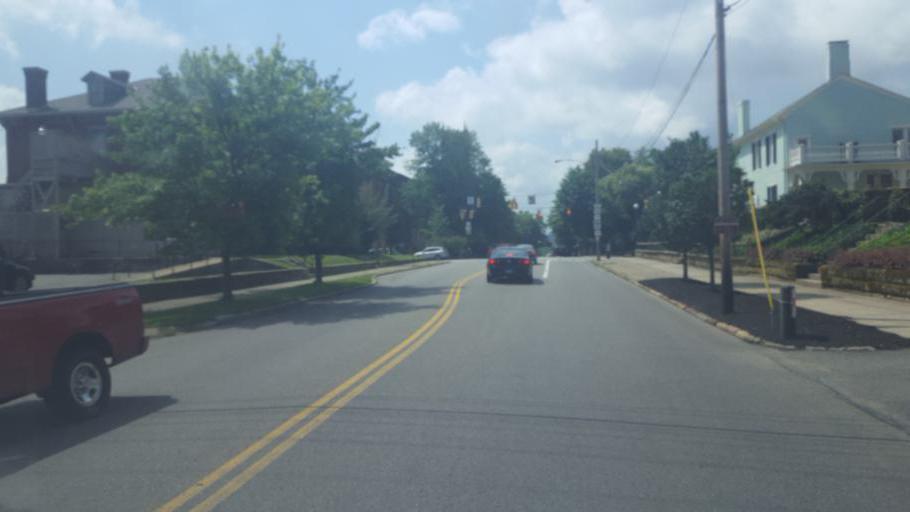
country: US
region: Ohio
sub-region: Fairfield County
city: Lancaster
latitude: 39.7144
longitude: -82.5993
